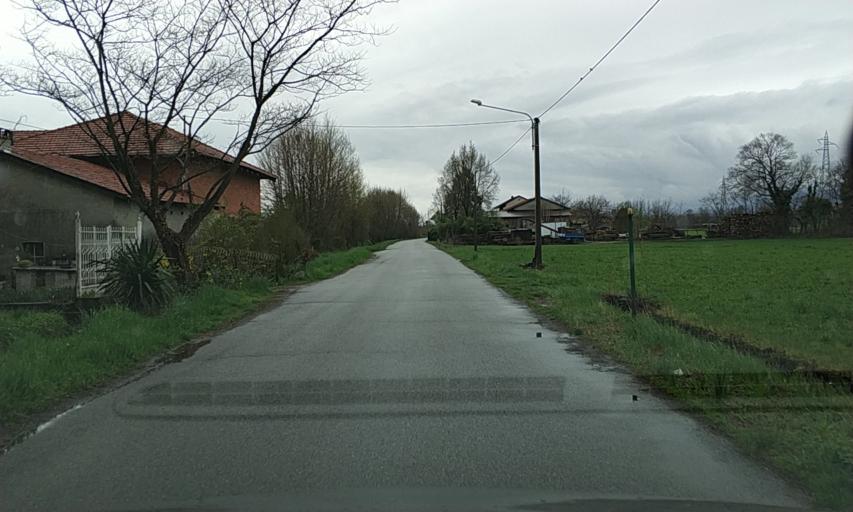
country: IT
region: Piedmont
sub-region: Provincia di Torino
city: Nole
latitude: 45.2355
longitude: 7.5755
